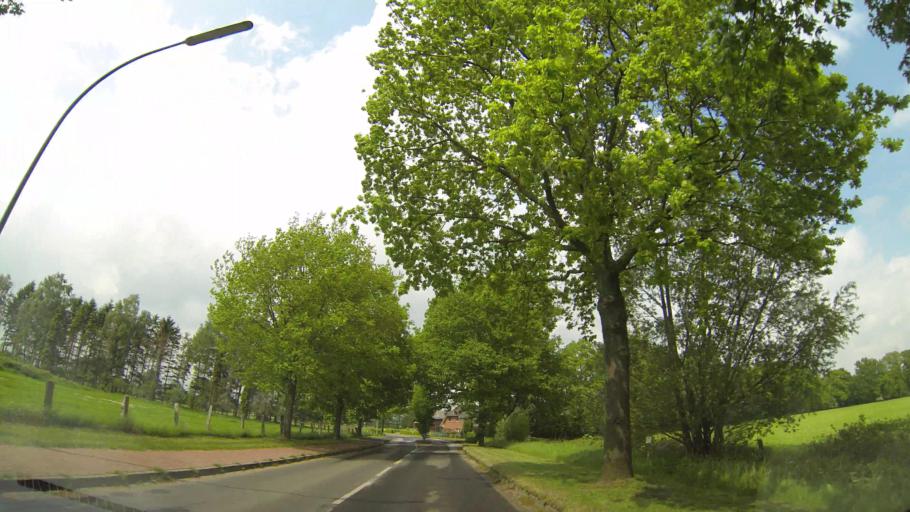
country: DE
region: Schleswig-Holstein
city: Ellerbek
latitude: 53.6606
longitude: 9.8632
